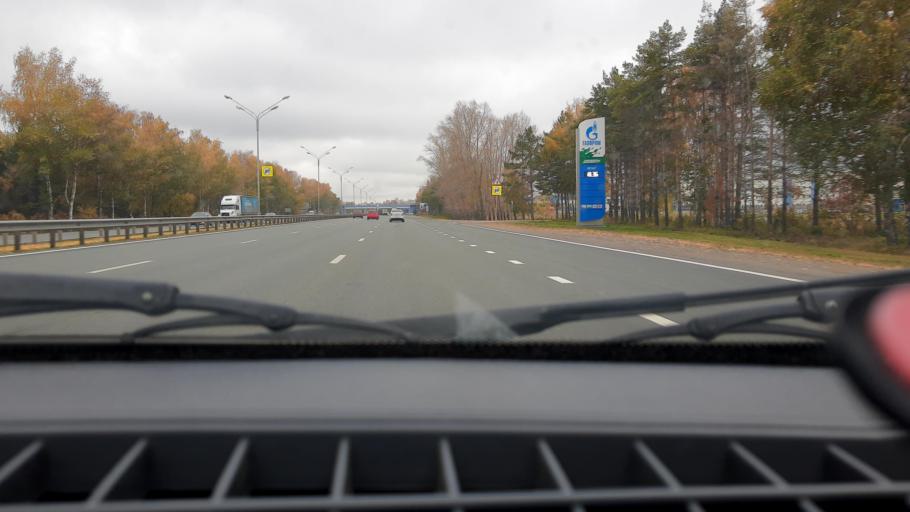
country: RU
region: Bashkortostan
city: Ufa
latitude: 54.5931
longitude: 55.9125
